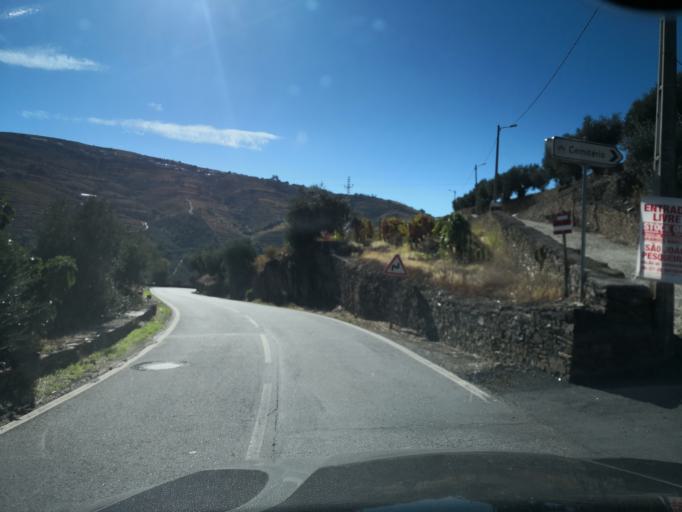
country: PT
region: Viseu
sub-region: Tabuaco
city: Tabuaco
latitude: 41.1707
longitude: -7.5426
